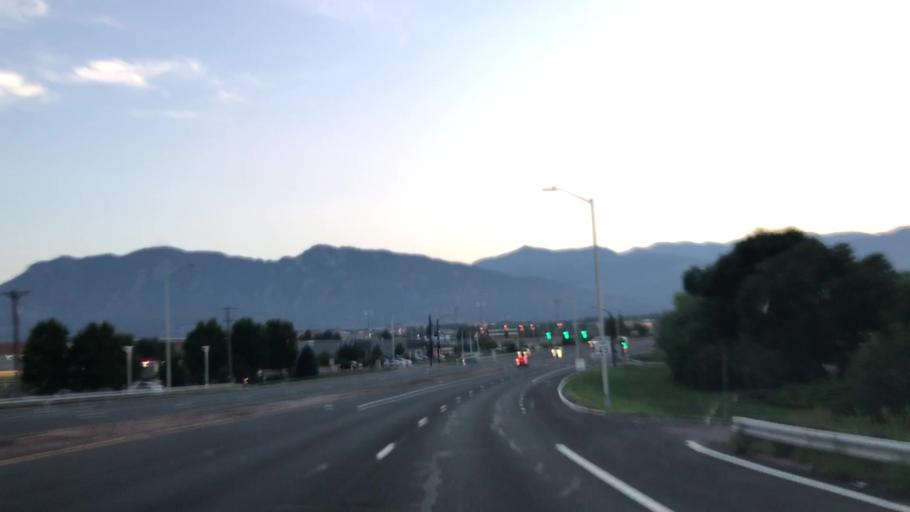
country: US
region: Colorado
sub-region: El Paso County
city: Stratmoor
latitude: 38.7963
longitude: -104.7882
